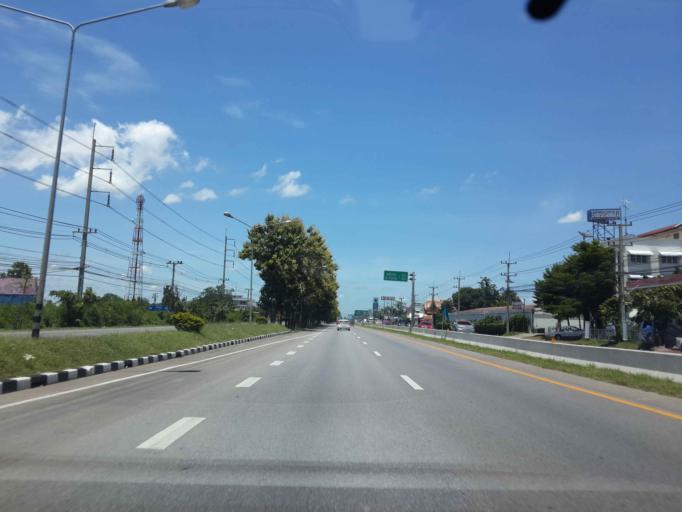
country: TH
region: Phetchaburi
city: Khao Yoi
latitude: 13.2992
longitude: 99.8237
